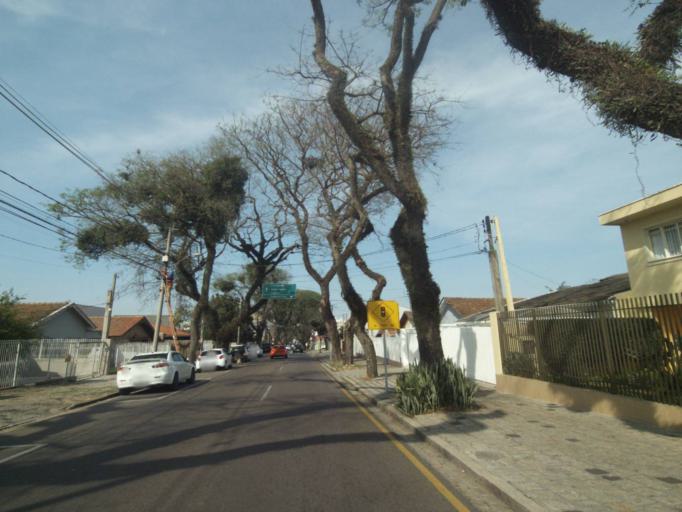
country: BR
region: Parana
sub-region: Curitiba
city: Curitiba
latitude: -25.4584
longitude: -49.3078
